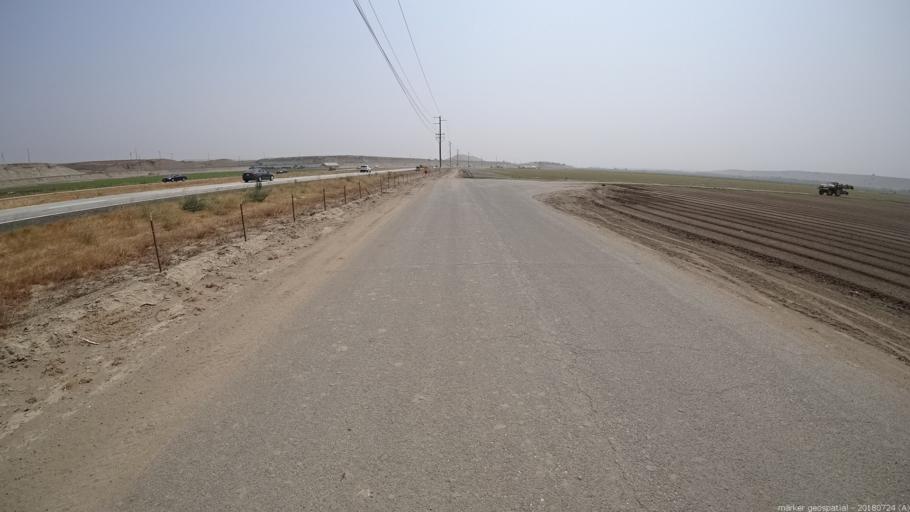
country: US
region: California
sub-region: Monterey County
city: King City
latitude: 36.1827
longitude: -121.0674
